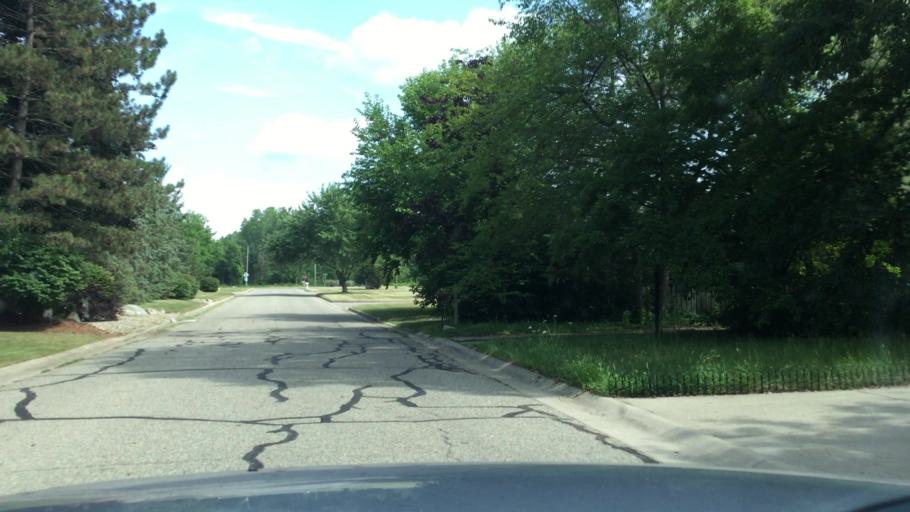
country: US
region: Michigan
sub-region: Genesee County
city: Flushing
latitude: 43.0583
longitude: -83.7884
